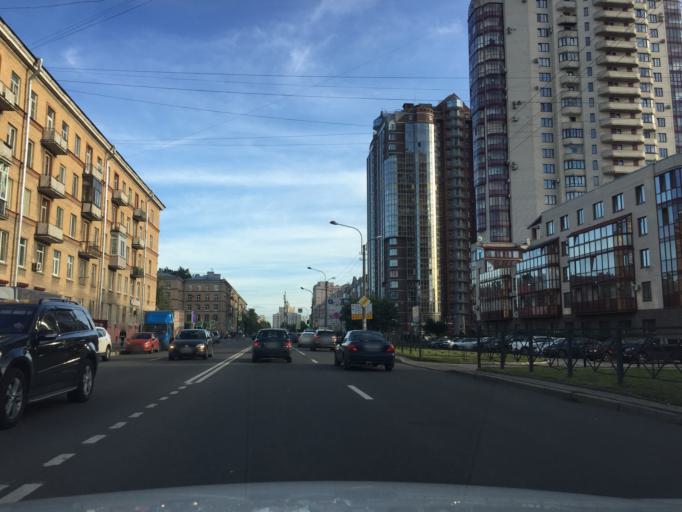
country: RU
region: St.-Petersburg
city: Kupchino
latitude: 59.8534
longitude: 30.3146
